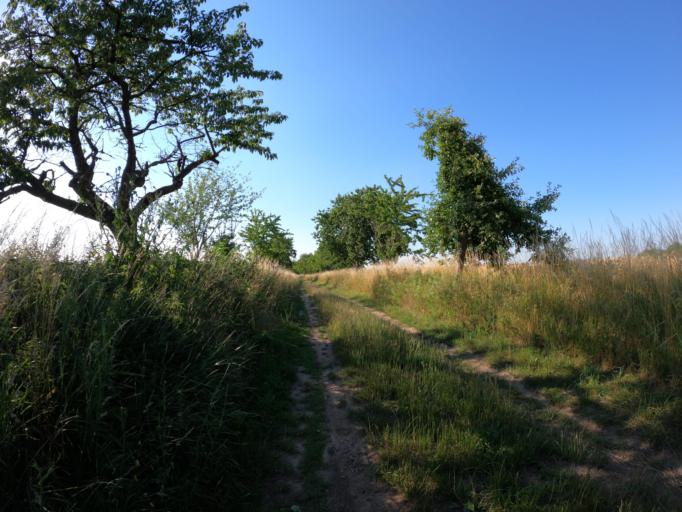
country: DE
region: Brandenburg
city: Tantow
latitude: 53.2422
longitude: 14.3695
